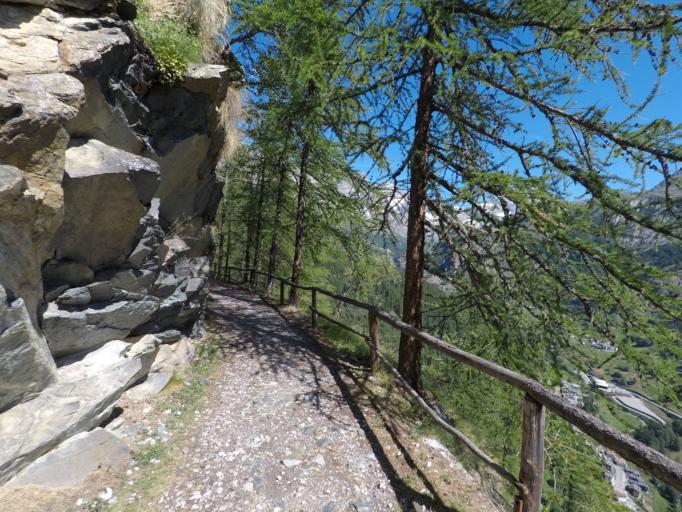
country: IT
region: Aosta Valley
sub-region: Valle d'Aosta
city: Valtournenche
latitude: 45.8798
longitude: 7.6181
